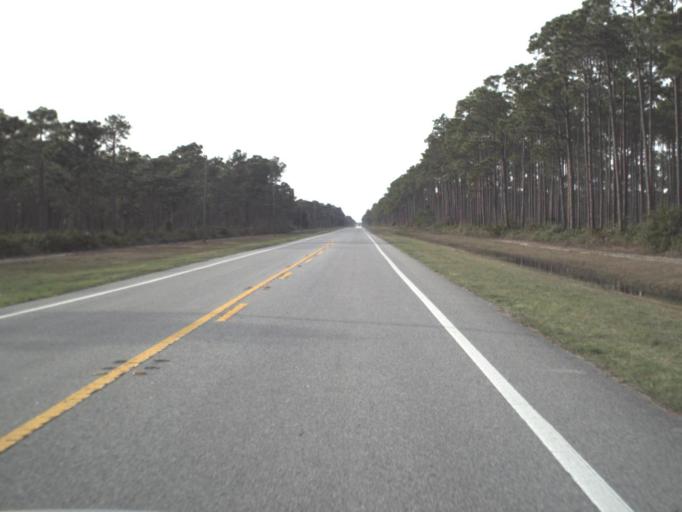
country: US
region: Florida
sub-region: Bay County
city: Tyndall Air Force Base
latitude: 30.0322
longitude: -85.5412
